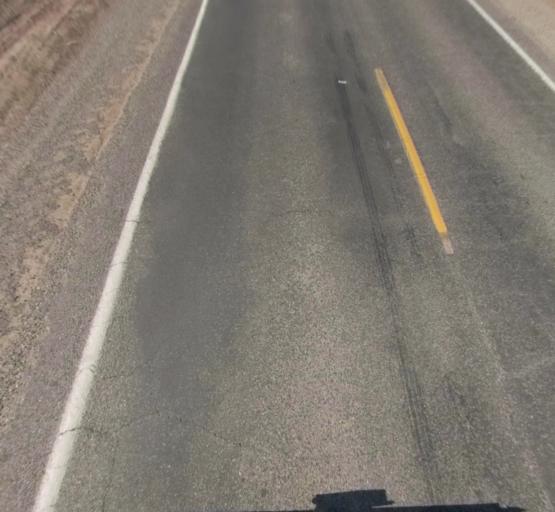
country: US
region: California
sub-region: Madera County
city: Fairmead
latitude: 37.0432
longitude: -120.2568
